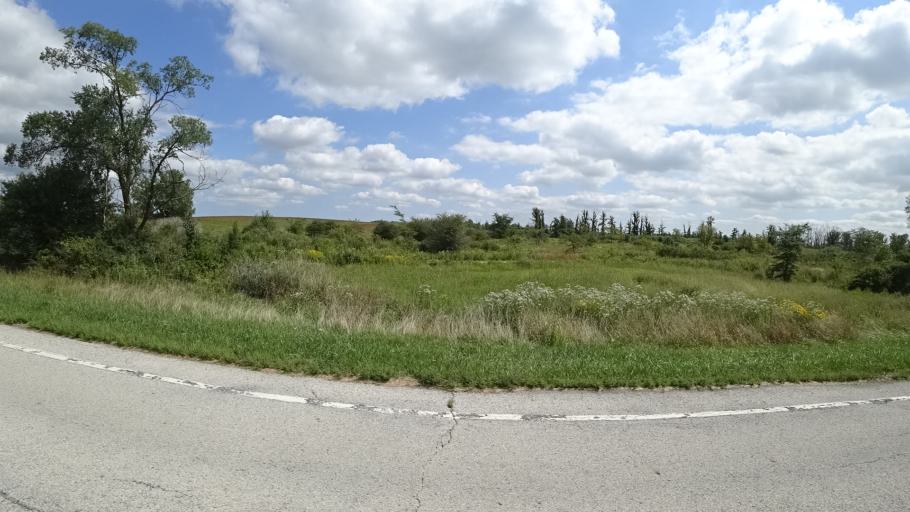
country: US
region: Illinois
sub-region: Cook County
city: Orland Hills
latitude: 41.5707
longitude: -87.8711
